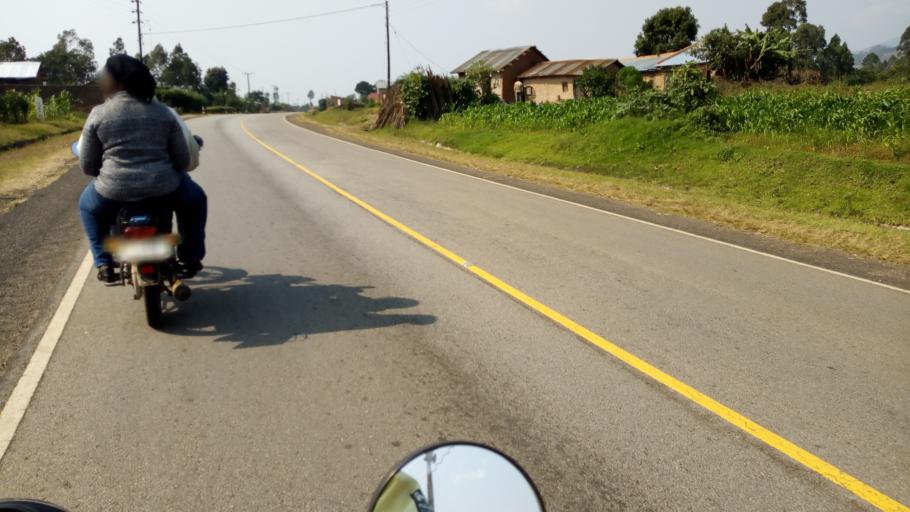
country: UG
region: Western Region
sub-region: Kisoro District
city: Kisoro
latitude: -1.3008
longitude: 29.7224
